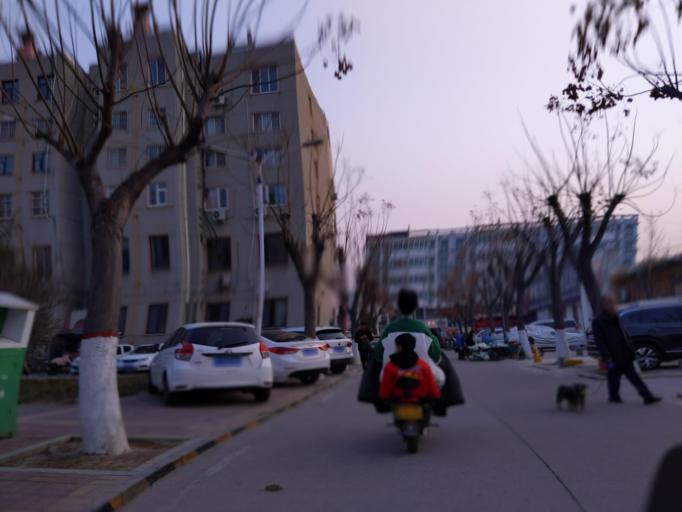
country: CN
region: Henan Sheng
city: Zhongyuanlu
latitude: 35.7712
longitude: 115.0884
